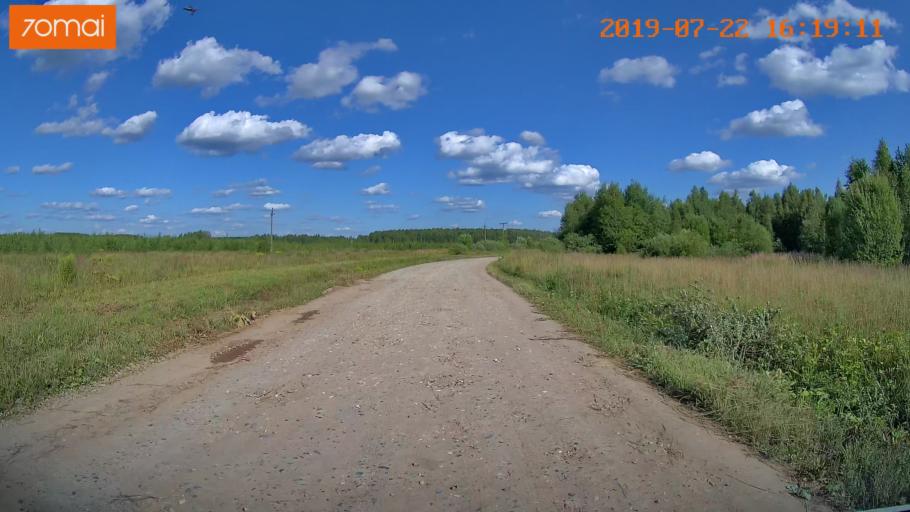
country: RU
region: Ivanovo
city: Novo-Talitsy
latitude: 57.0665
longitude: 40.8901
